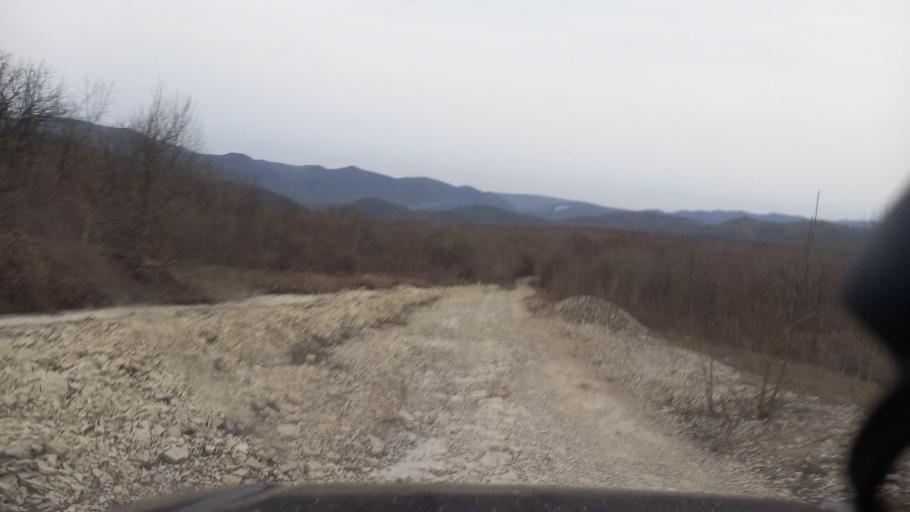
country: RU
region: Krasnodarskiy
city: Pshada
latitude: 44.5945
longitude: 38.3004
